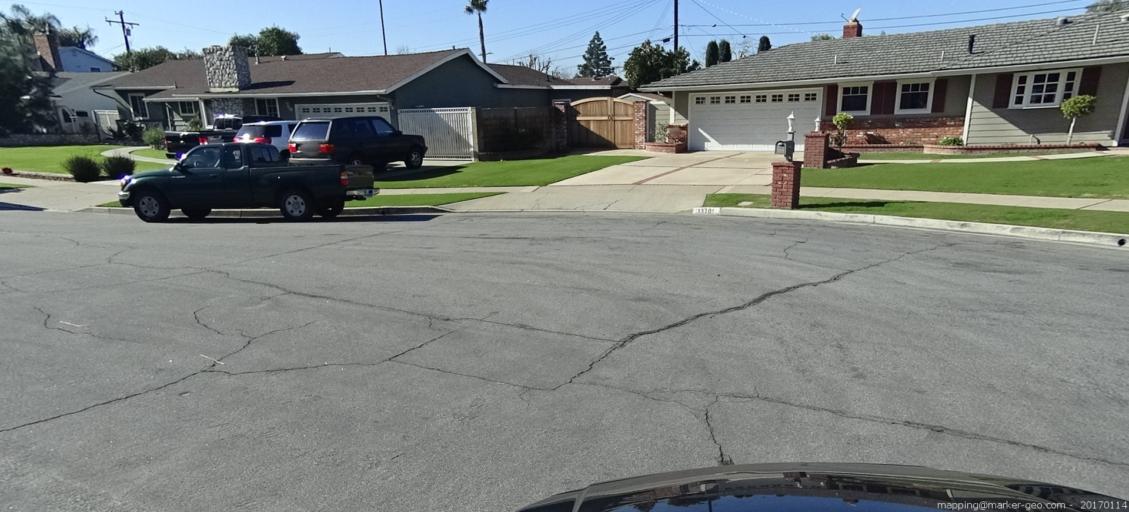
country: US
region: California
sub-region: Orange County
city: North Tustin
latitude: 33.7642
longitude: -117.8025
